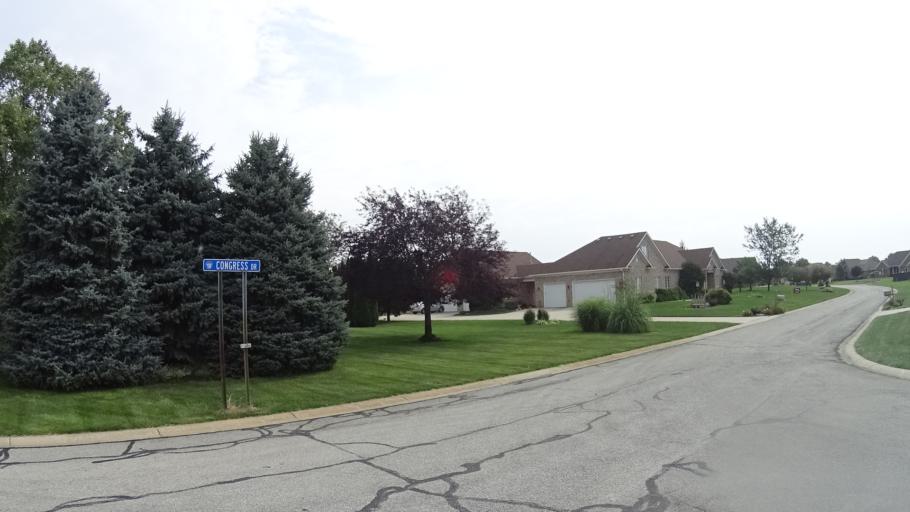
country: US
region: Indiana
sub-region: Madison County
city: Pendleton
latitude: 40.0119
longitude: -85.7948
